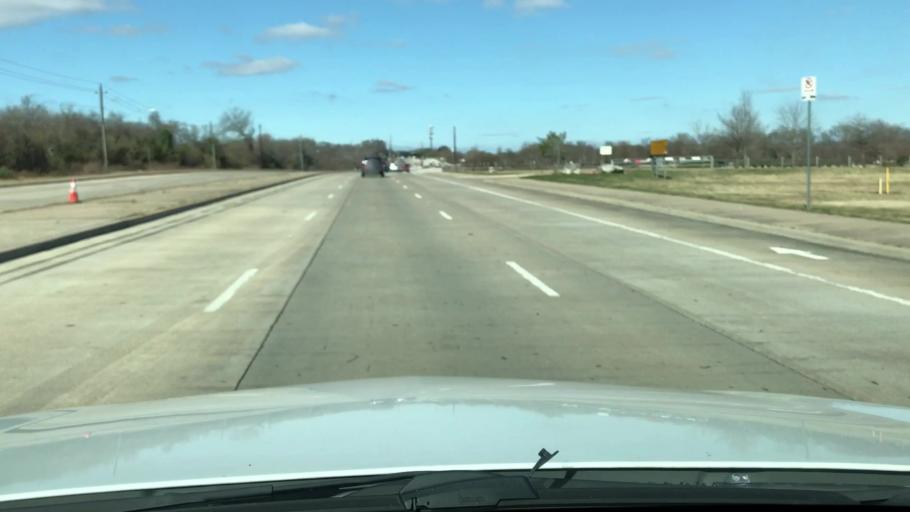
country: US
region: Texas
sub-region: Travis County
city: Onion Creek
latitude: 30.1744
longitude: -97.7424
